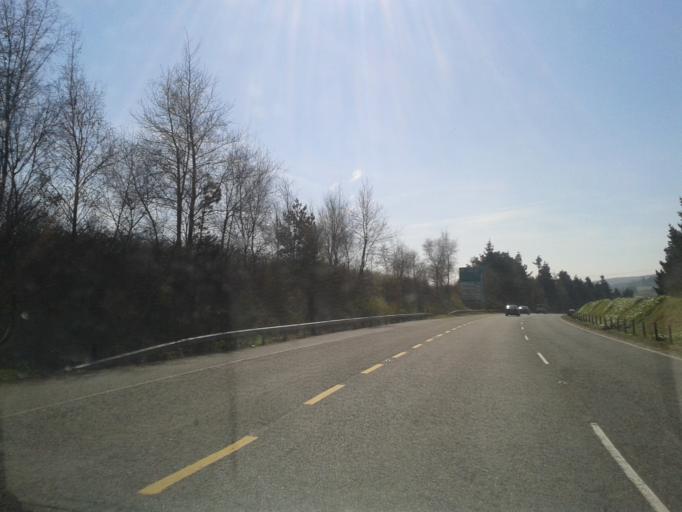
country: IE
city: Kilquade
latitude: 53.0829
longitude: -6.0892
